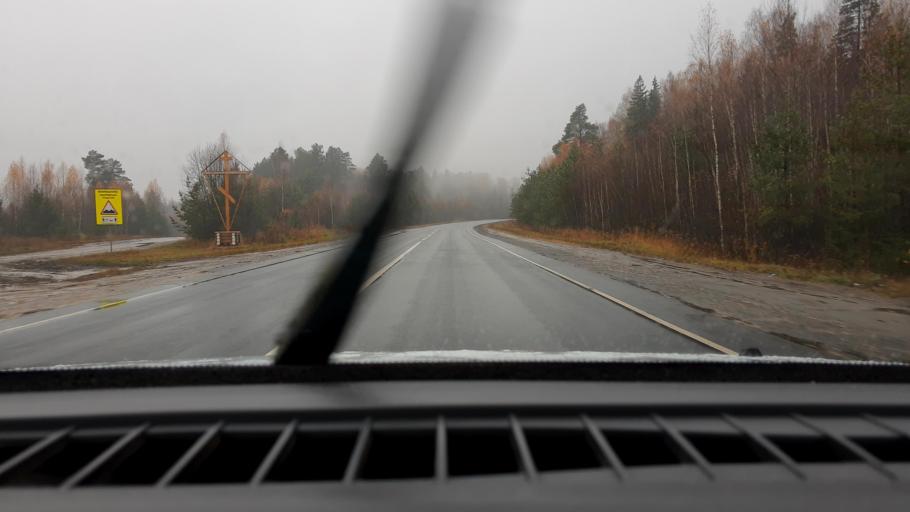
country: RU
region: Nizjnij Novgorod
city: Linda
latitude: 56.6968
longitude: 44.2077
